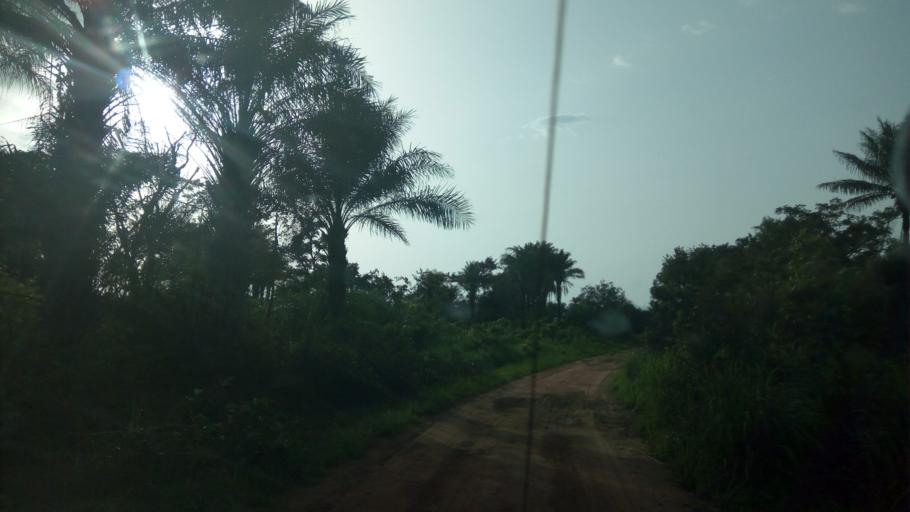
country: SL
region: Northern Province
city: Mambolo
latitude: 9.0157
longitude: -13.0157
